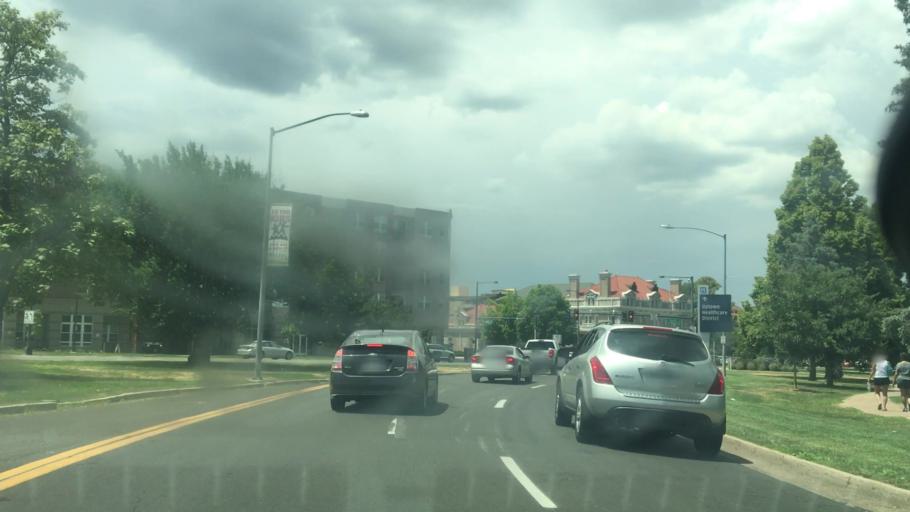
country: US
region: Colorado
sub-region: Denver County
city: Denver
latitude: 39.7440
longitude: -104.9588
